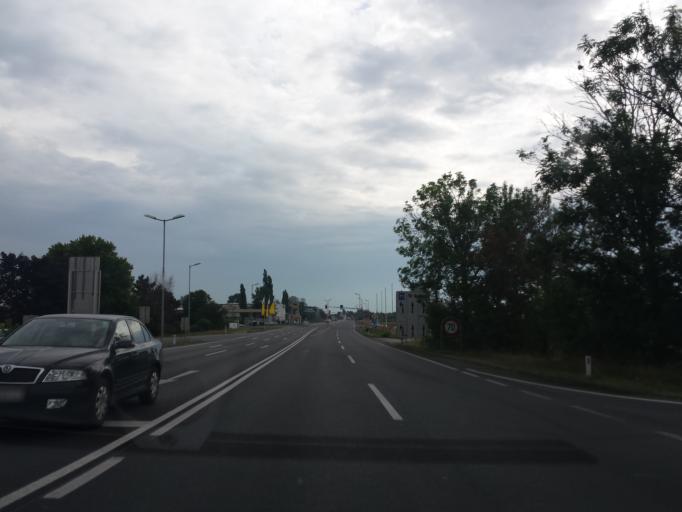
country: AT
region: Lower Austria
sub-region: Politischer Bezirk Baden
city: Traiskirchen
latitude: 47.9988
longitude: 16.3004
